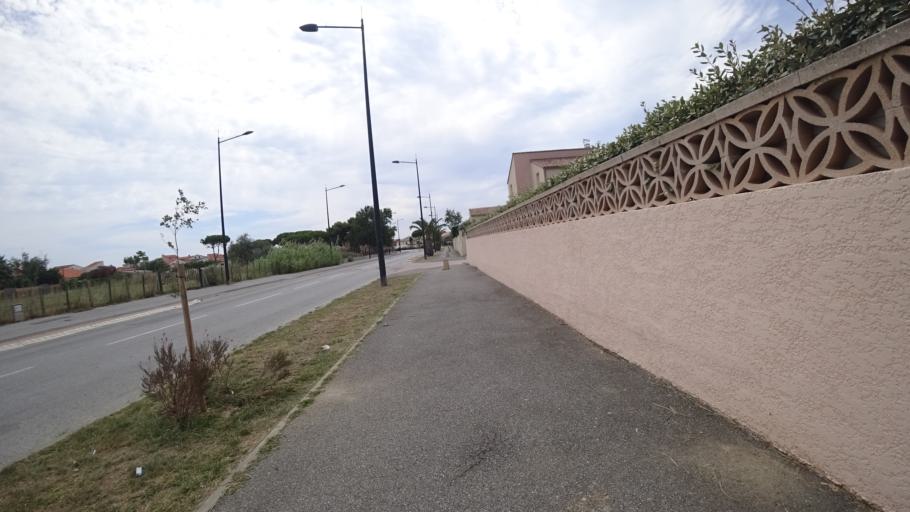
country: FR
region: Languedoc-Roussillon
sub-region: Departement des Pyrenees-Orientales
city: Le Barcares
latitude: 42.7957
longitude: 3.0316
